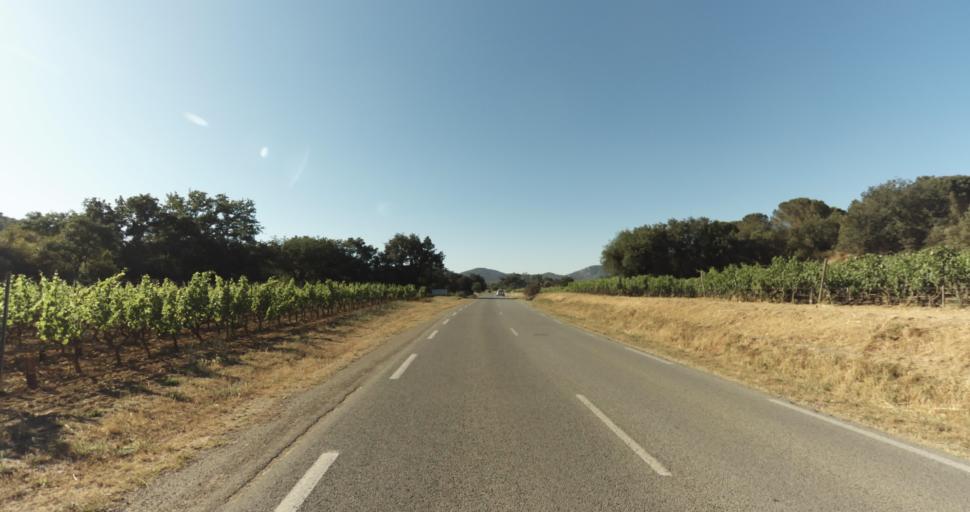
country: FR
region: Provence-Alpes-Cote d'Azur
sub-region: Departement du Var
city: Gassin
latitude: 43.2450
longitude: 6.5948
